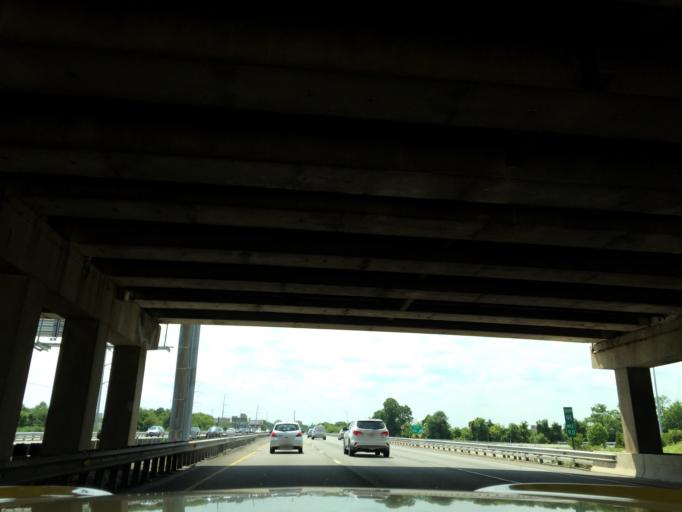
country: US
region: Pennsylvania
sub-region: Delaware County
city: Prospect Park
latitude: 39.8711
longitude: -75.3010
